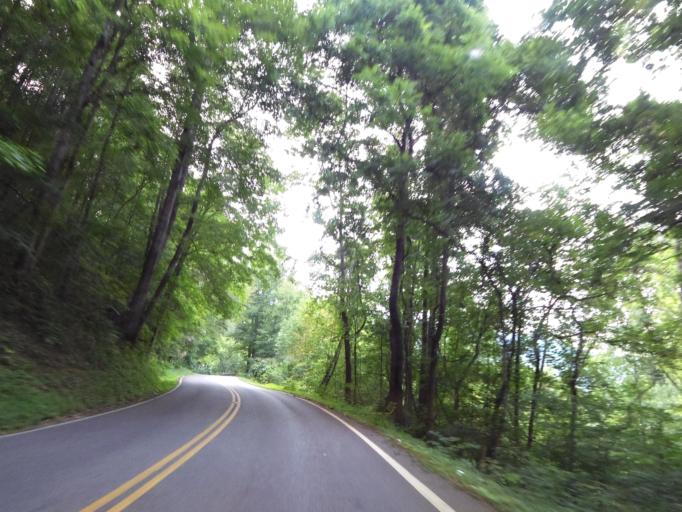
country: US
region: Tennessee
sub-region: Anderson County
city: Rocky Top
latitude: 36.1820
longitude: -84.1829
